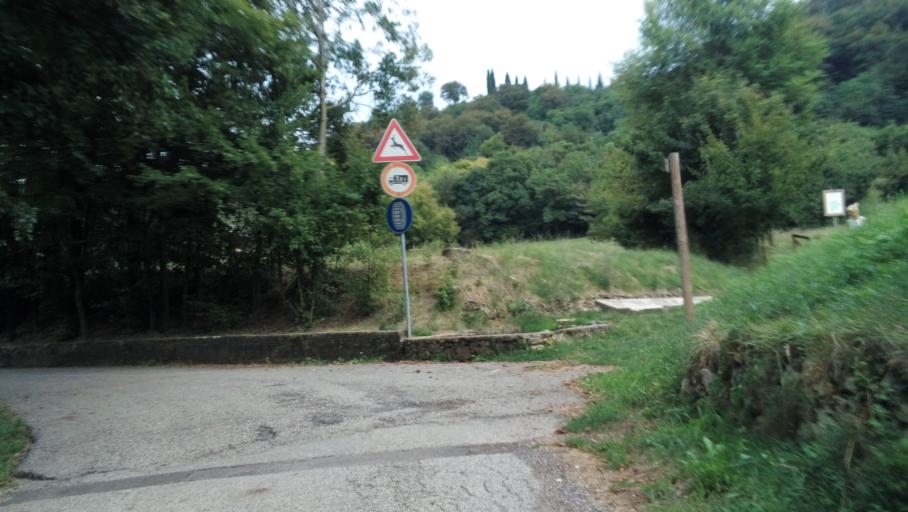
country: IT
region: Veneto
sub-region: Provincia di Vicenza
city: Monteviale
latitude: 45.5534
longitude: 11.4579
